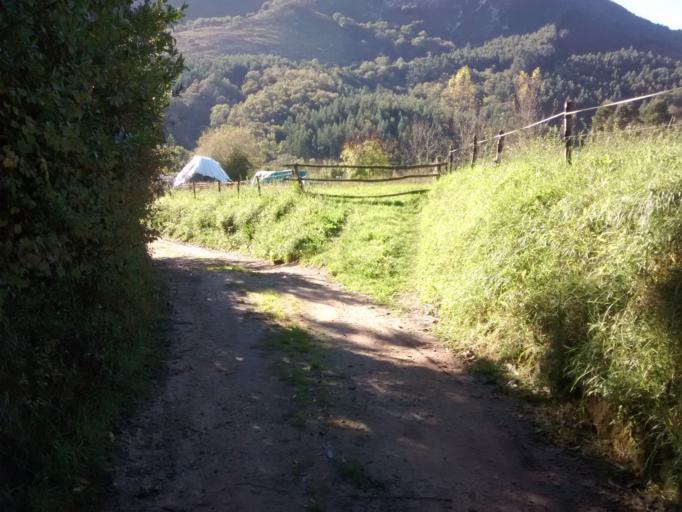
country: ES
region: Asturias
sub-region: Province of Asturias
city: Colunga
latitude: 43.4657
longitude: -5.2369
